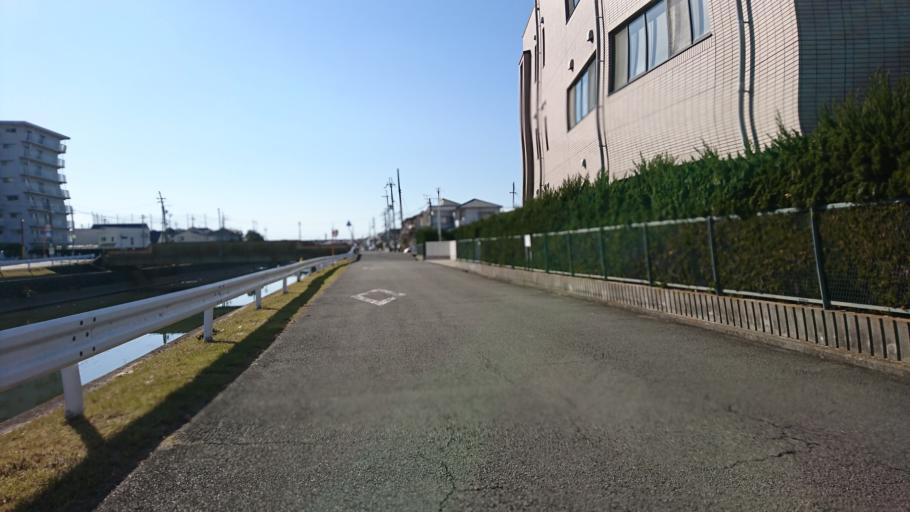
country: JP
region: Hyogo
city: Kakogawacho-honmachi
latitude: 34.7514
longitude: 134.8383
